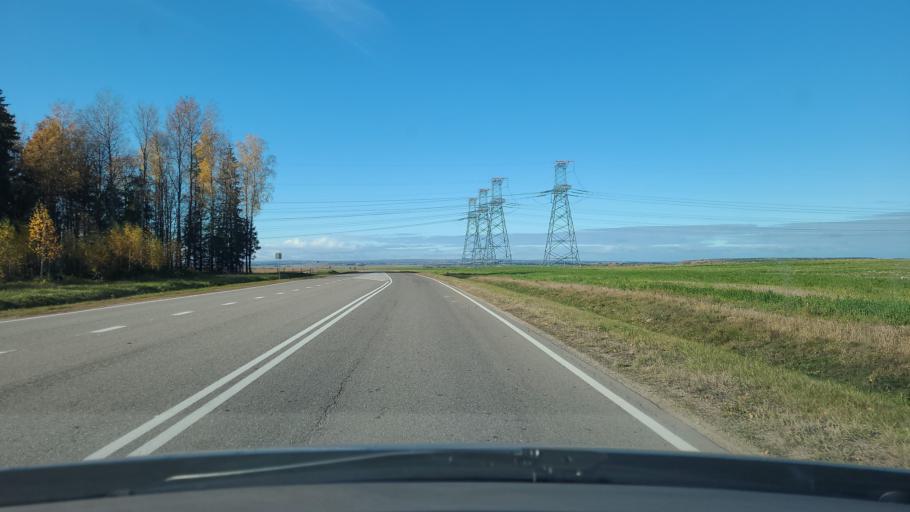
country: BY
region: Grodnenskaya
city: Astravyets
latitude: 54.7673
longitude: 26.0817
